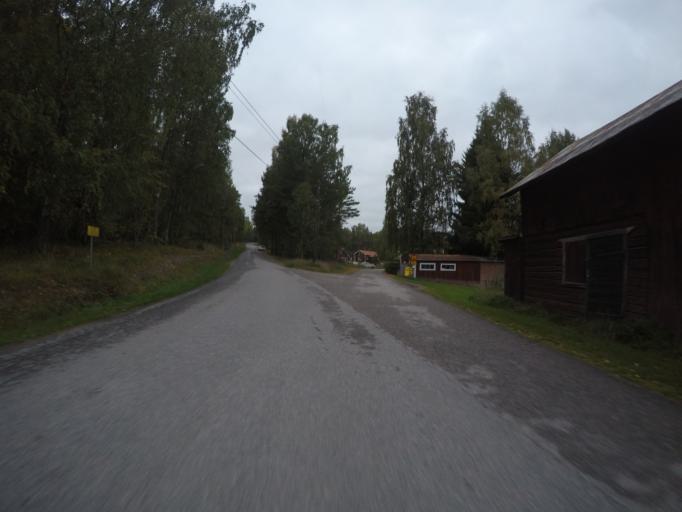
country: SE
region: Vaestmanland
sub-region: Kungsors Kommun
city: Kungsoer
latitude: 59.4079
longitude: 16.1129
